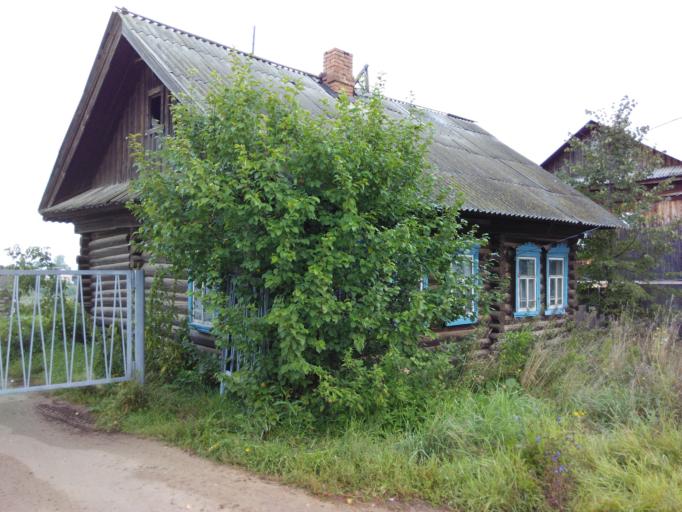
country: RU
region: Perm
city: Foki
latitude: 56.6914
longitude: 54.3473
